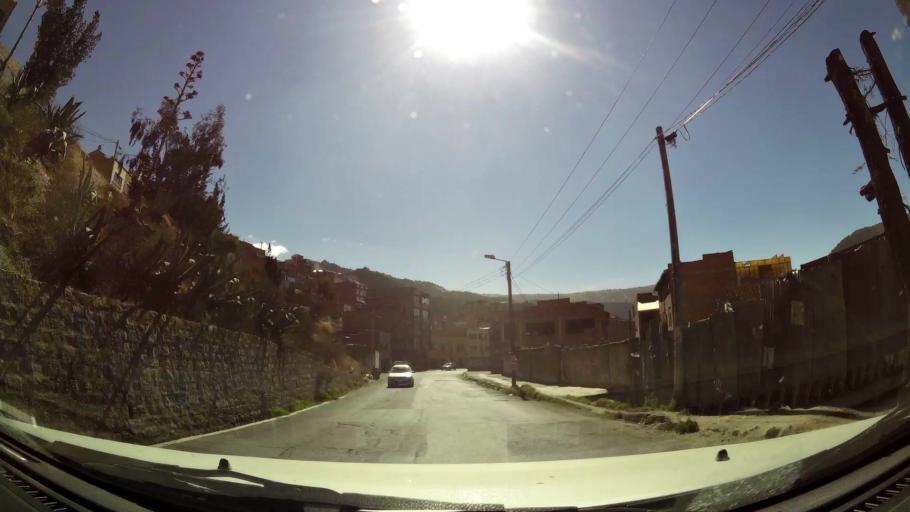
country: BO
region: La Paz
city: La Paz
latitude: -16.4897
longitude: -68.1473
